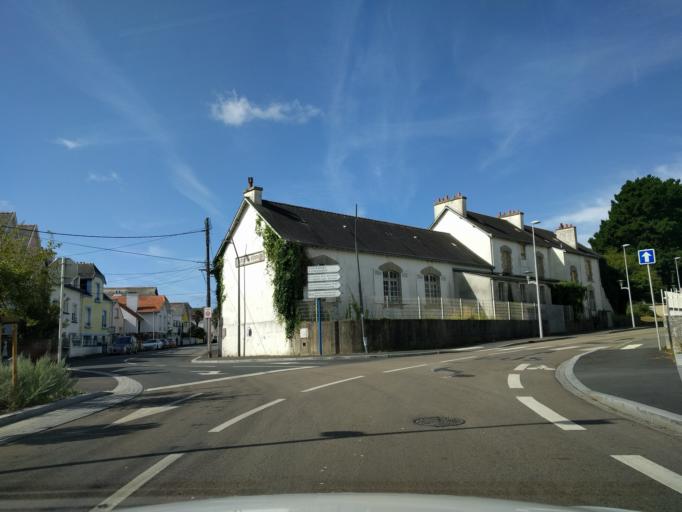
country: FR
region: Brittany
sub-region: Departement du Morbihan
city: Lorient
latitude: 47.7430
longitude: -3.3891
